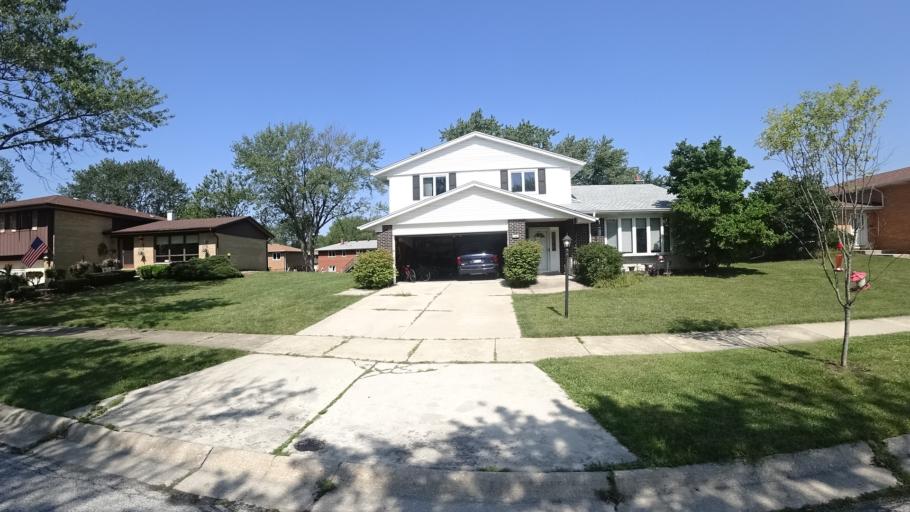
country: US
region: Illinois
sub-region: Cook County
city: Oak Forest
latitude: 41.6133
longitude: -87.7809
